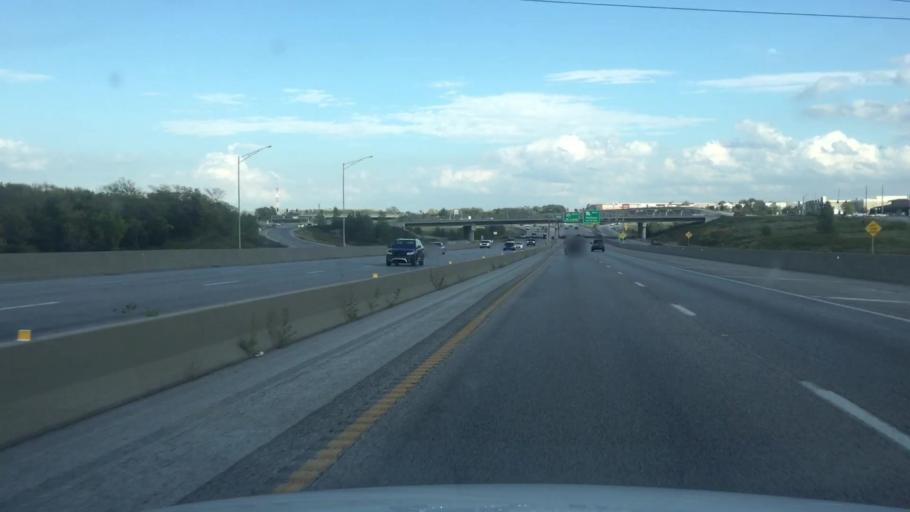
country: US
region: Missouri
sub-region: Jackson County
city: Lees Summit
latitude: 38.9340
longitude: -94.4163
